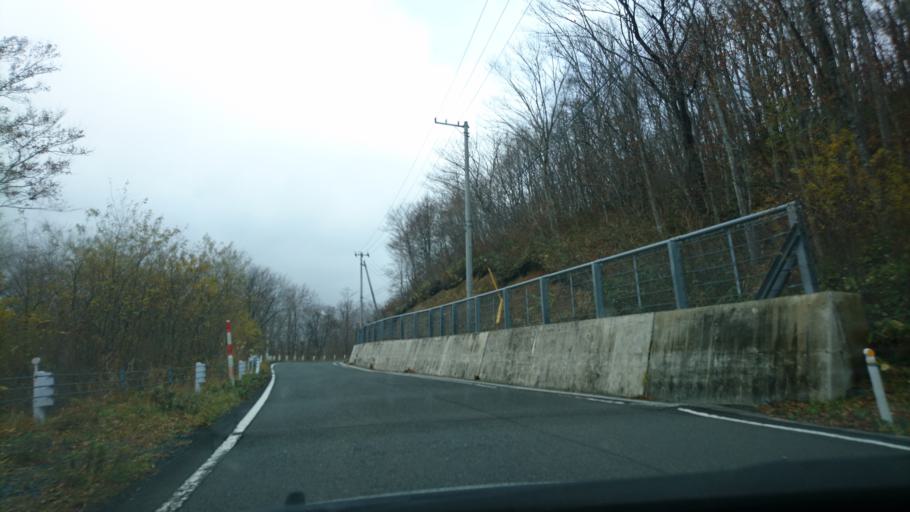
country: JP
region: Iwate
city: Ichinoseki
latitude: 38.9218
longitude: 140.8436
